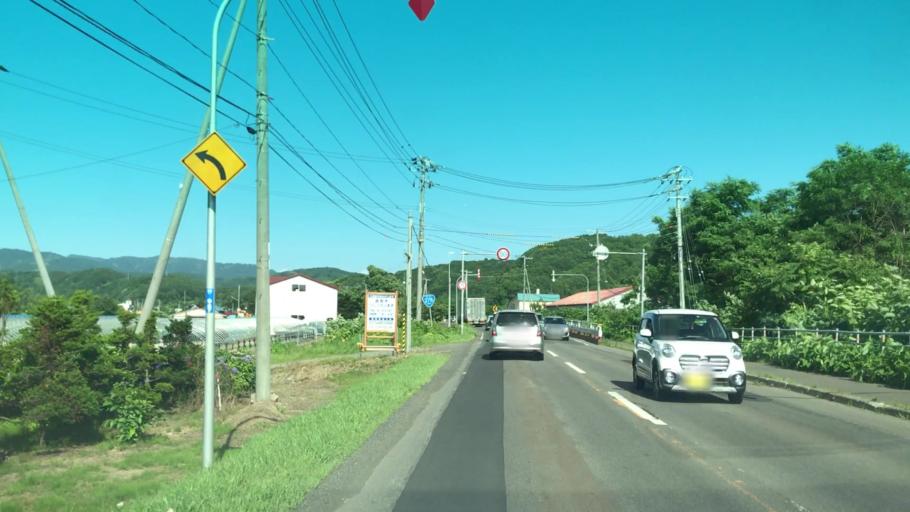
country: JP
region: Hokkaido
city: Iwanai
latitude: 42.9774
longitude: 140.6347
